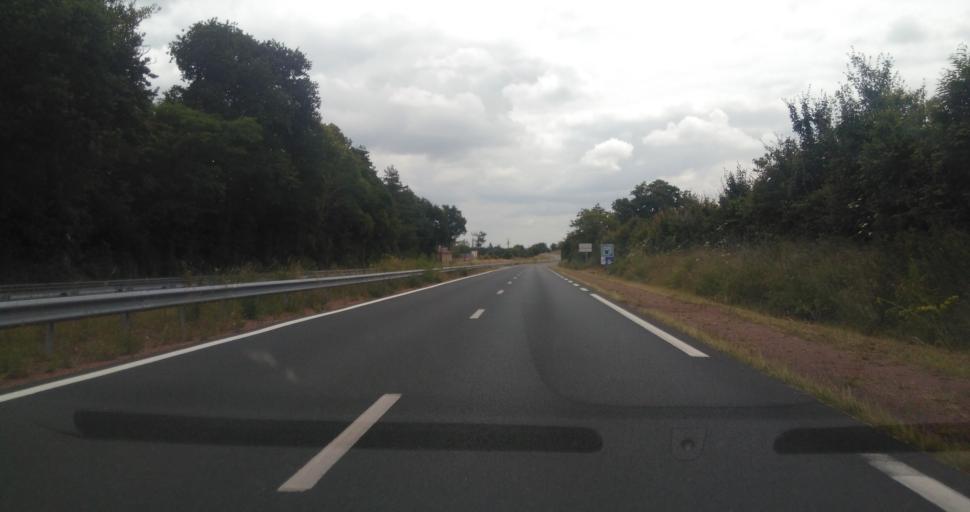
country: FR
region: Pays de la Loire
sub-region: Departement de la Vendee
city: Bournezeau
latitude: 46.6420
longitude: -1.1939
